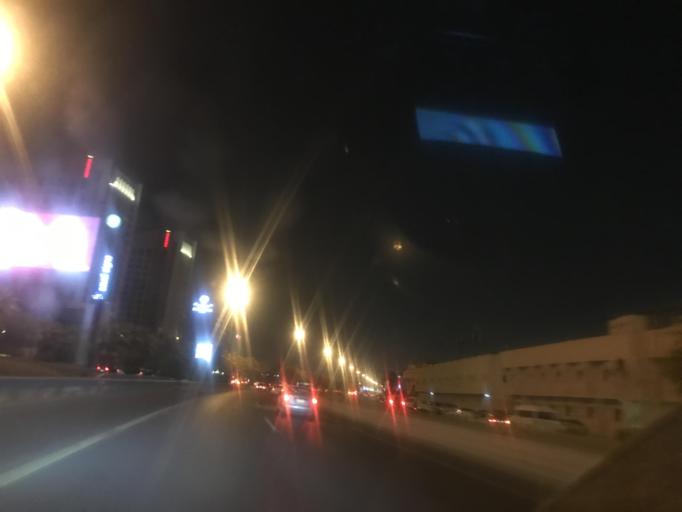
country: SA
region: Ar Riyad
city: Riyadh
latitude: 24.7624
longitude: 46.6517
